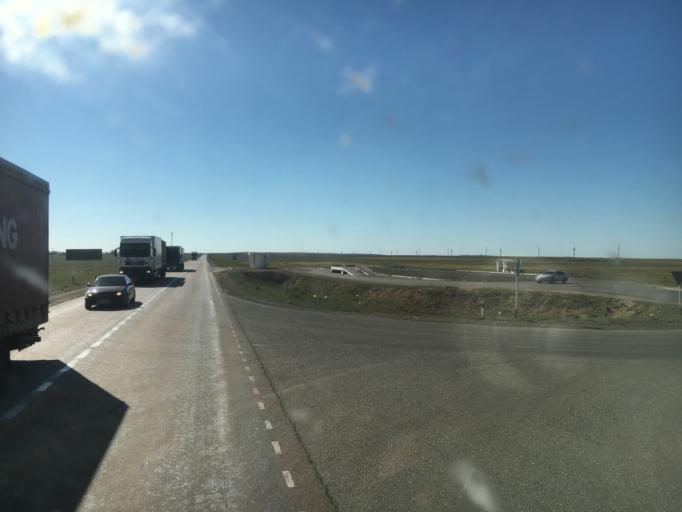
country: RU
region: Orenburg
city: Dombarovskiy
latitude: 50.0706
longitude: 59.6252
